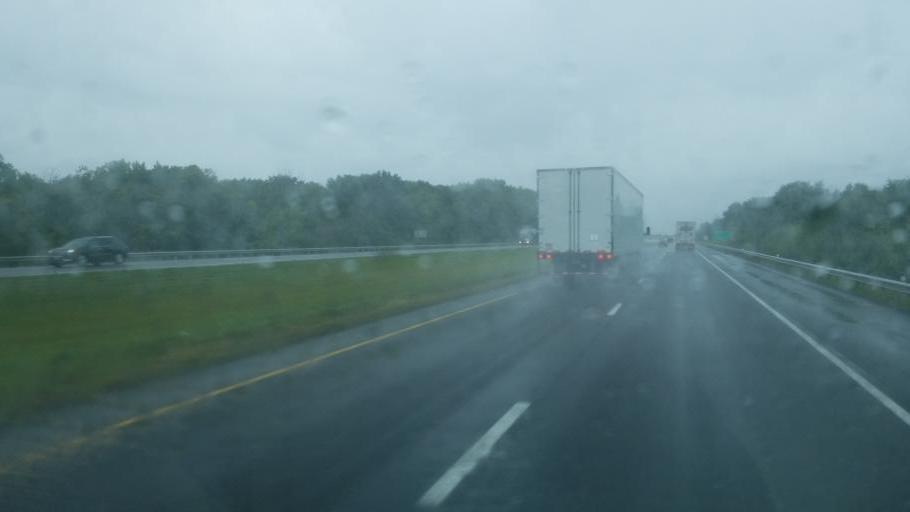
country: US
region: Ohio
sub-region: Summit County
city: Richfield
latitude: 41.2165
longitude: -81.6533
